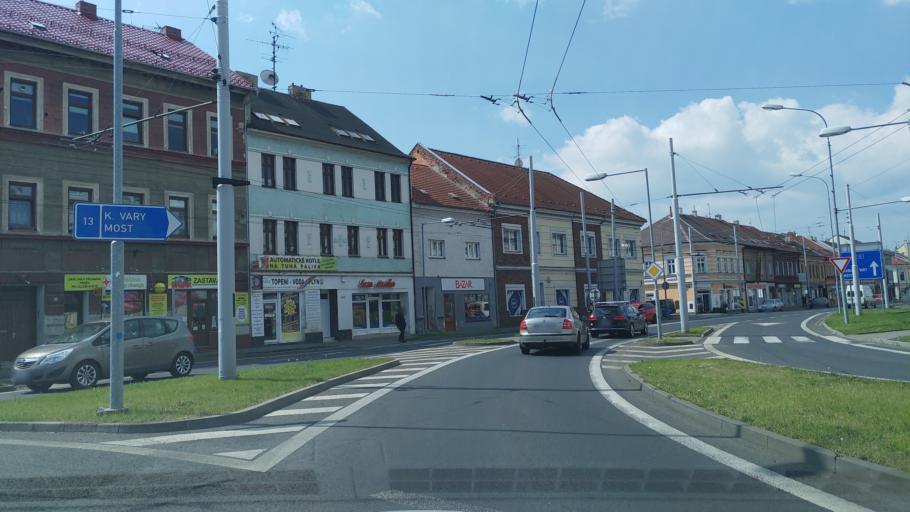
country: CZ
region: Ustecky
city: Probostov
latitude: 50.6529
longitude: 13.8459
